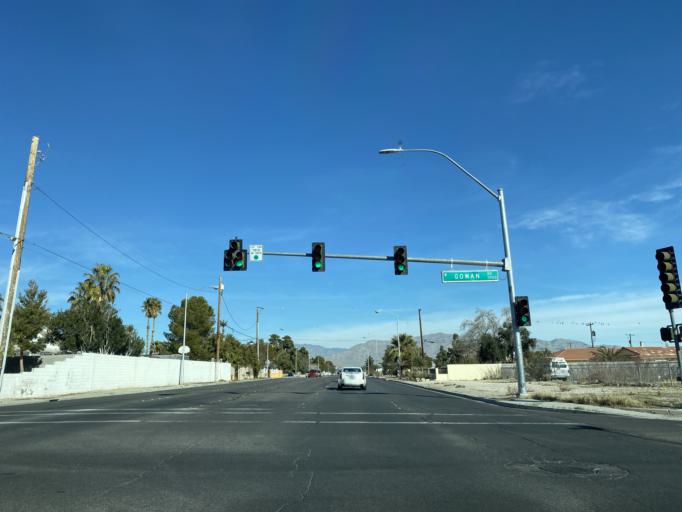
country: US
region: Nevada
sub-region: Clark County
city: Las Vegas
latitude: 36.2243
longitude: -115.2257
